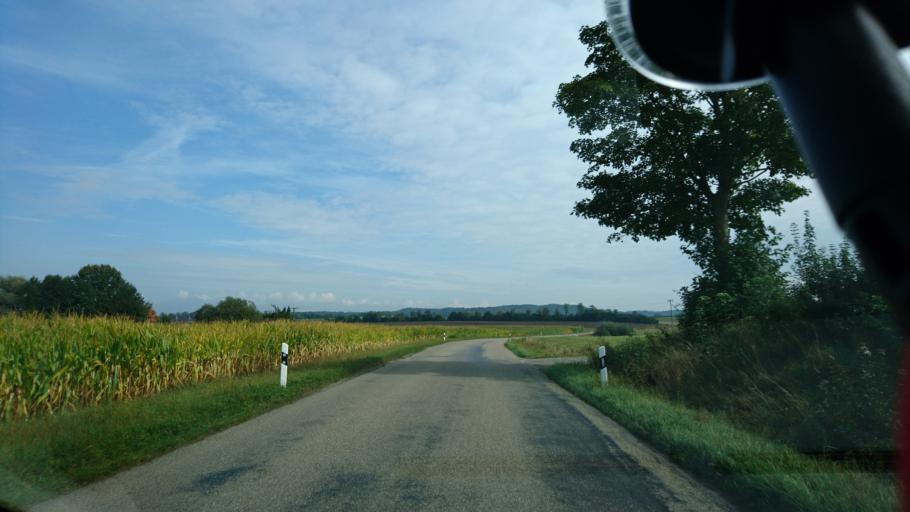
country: DE
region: Baden-Wuerttemberg
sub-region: Regierungsbezirk Stuttgart
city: Ilshofen
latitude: 49.1240
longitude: 9.9133
